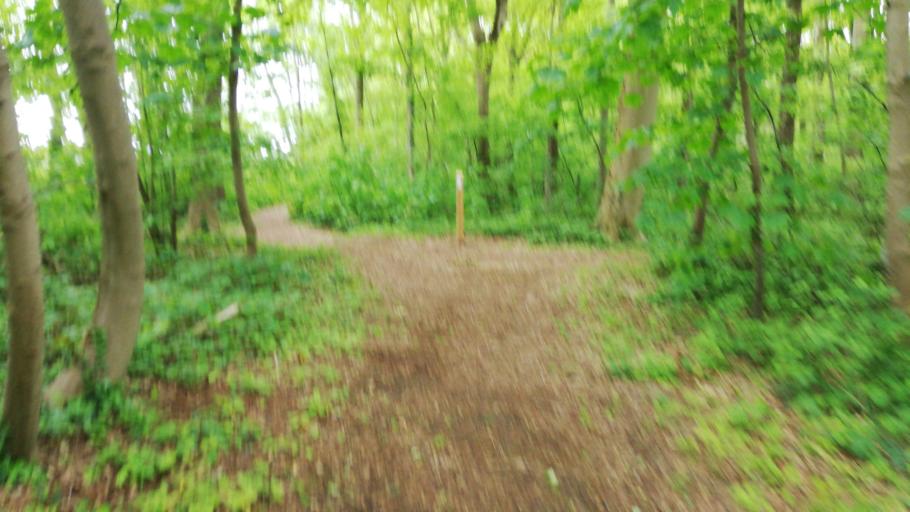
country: BE
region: Flanders
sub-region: Provincie West-Vlaanderen
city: Poperinge
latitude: 50.8832
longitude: 2.6985
